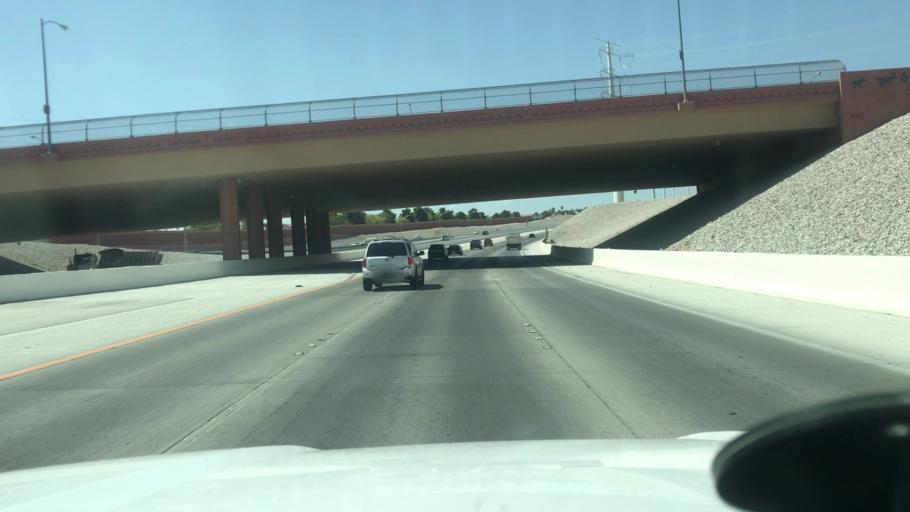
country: US
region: Nevada
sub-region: Clark County
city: Summerlin South
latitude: 36.2202
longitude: -115.3273
